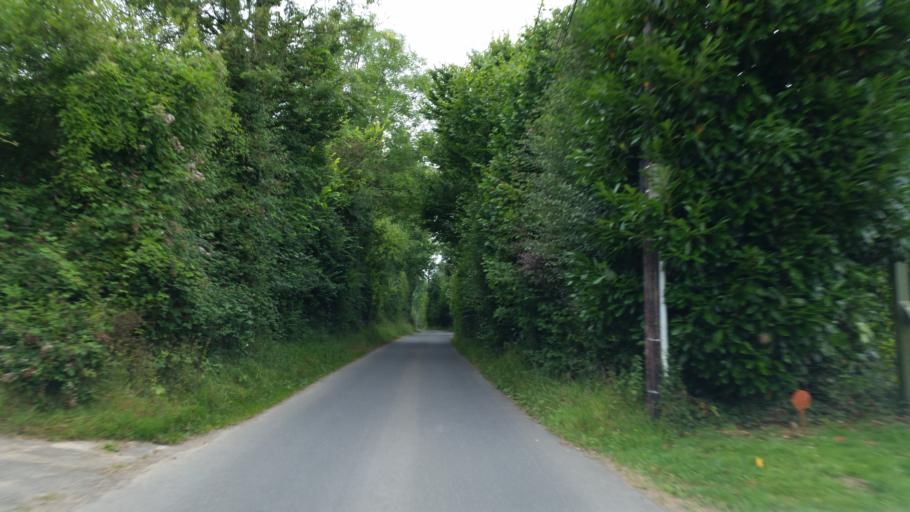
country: FR
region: Lower Normandy
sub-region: Departement du Calvados
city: Equemauville
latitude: 49.3920
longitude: 0.2325
